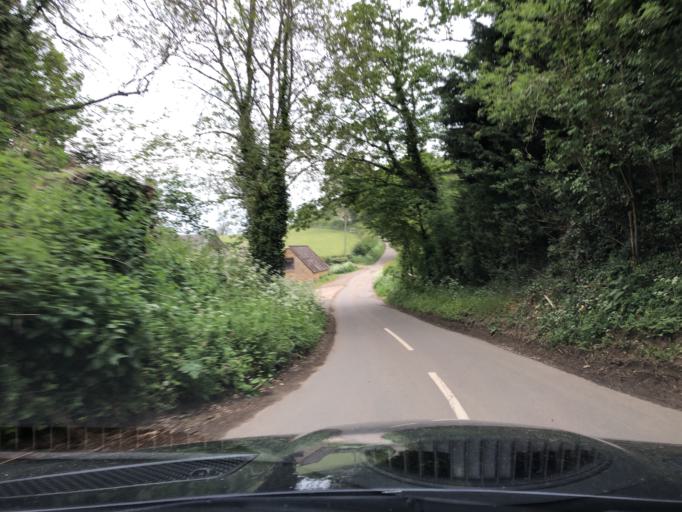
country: GB
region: England
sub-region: Oxfordshire
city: Claydon
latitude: 52.1428
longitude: -1.3715
